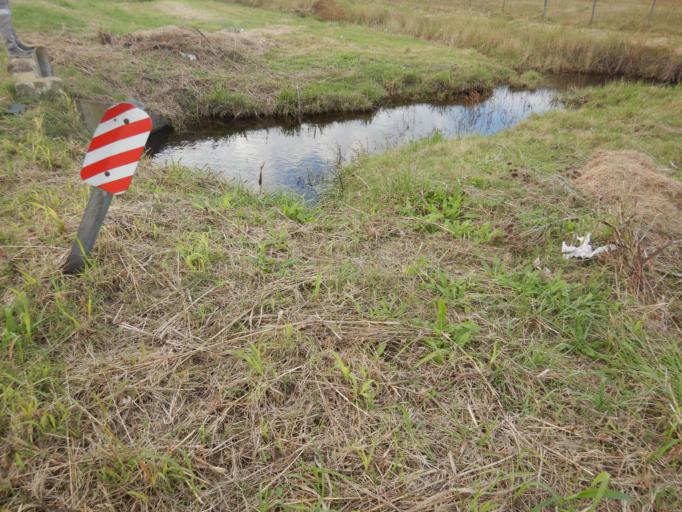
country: AR
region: Santa Fe
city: Roldan
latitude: -32.8996
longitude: -60.9421
